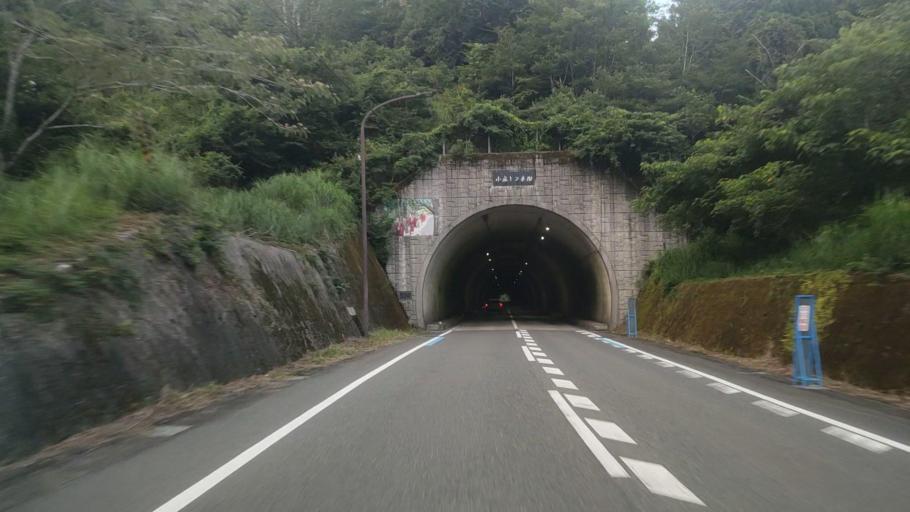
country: JP
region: Wakayama
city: Tanabe
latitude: 33.8344
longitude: 135.6555
